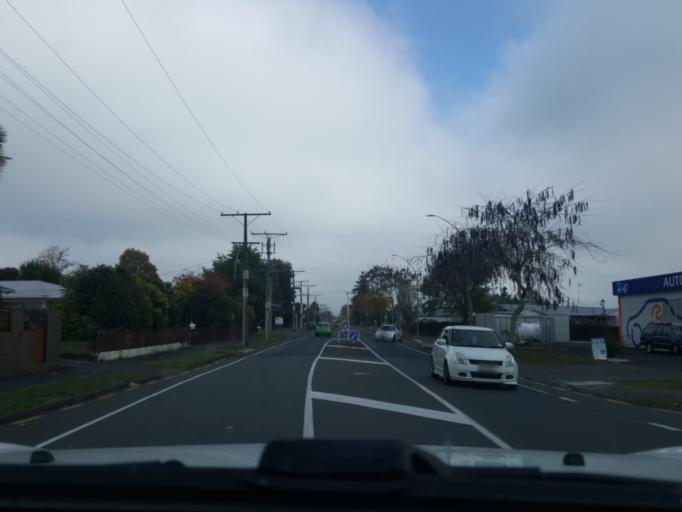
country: NZ
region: Waikato
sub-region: Hamilton City
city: Hamilton
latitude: -37.7519
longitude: 175.2790
